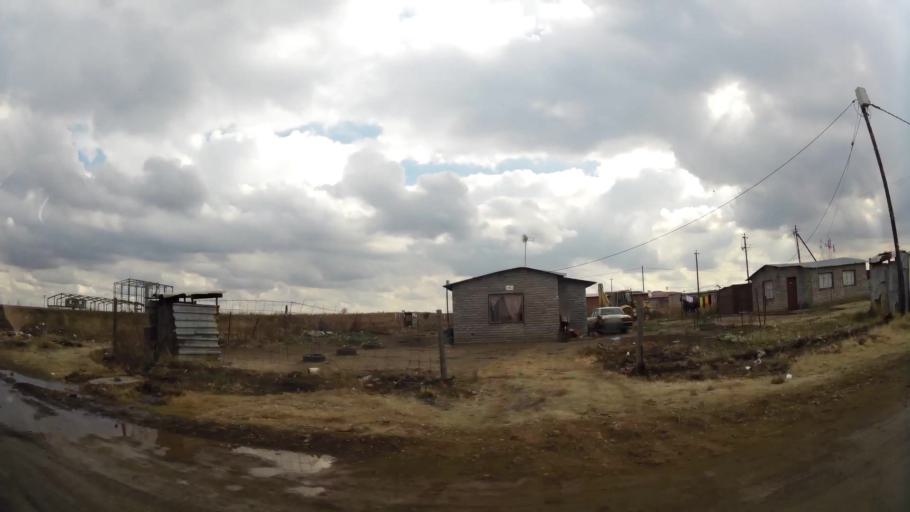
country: ZA
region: Orange Free State
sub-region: Fezile Dabi District Municipality
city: Sasolburg
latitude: -26.8657
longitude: 27.8945
